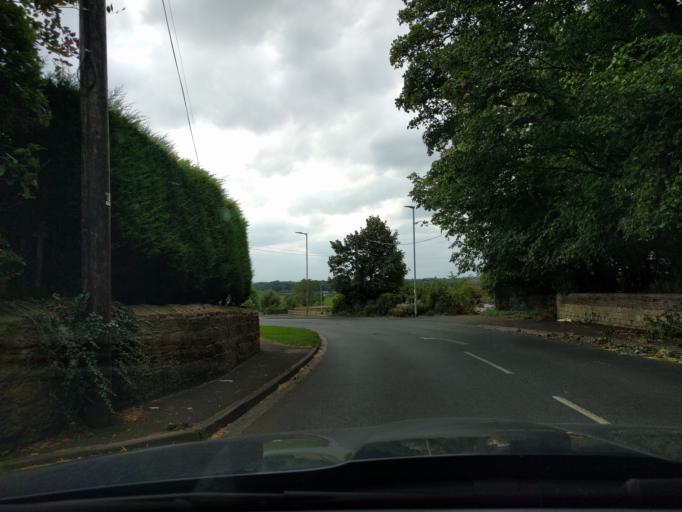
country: GB
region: England
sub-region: Northumberland
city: Choppington
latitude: 55.1308
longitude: -1.6361
